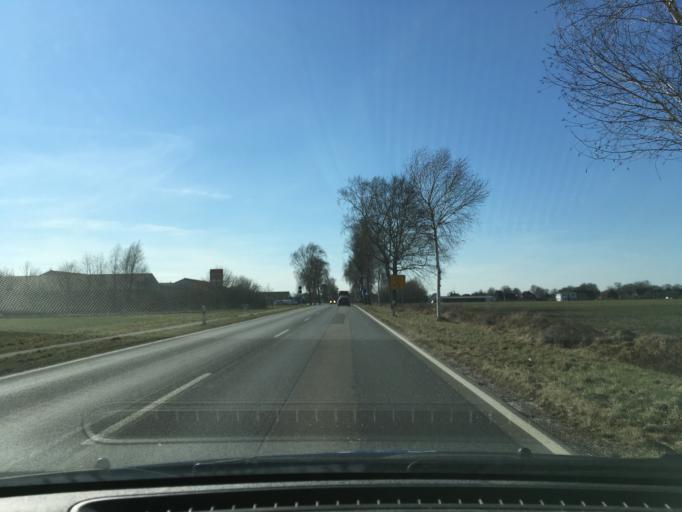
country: DE
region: Lower Saxony
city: Ottersberg
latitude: 53.0692
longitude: 9.0933
